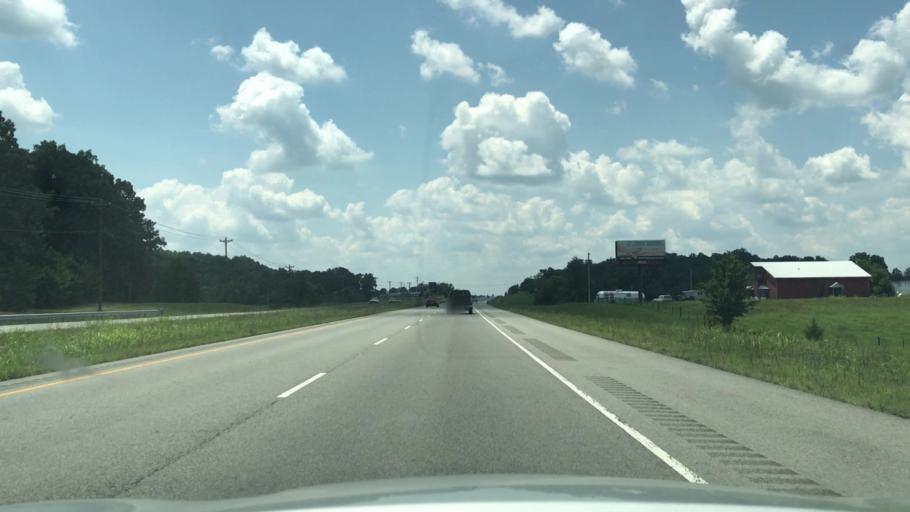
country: US
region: Tennessee
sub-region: Overton County
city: Livingston
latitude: 36.3063
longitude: -85.3667
